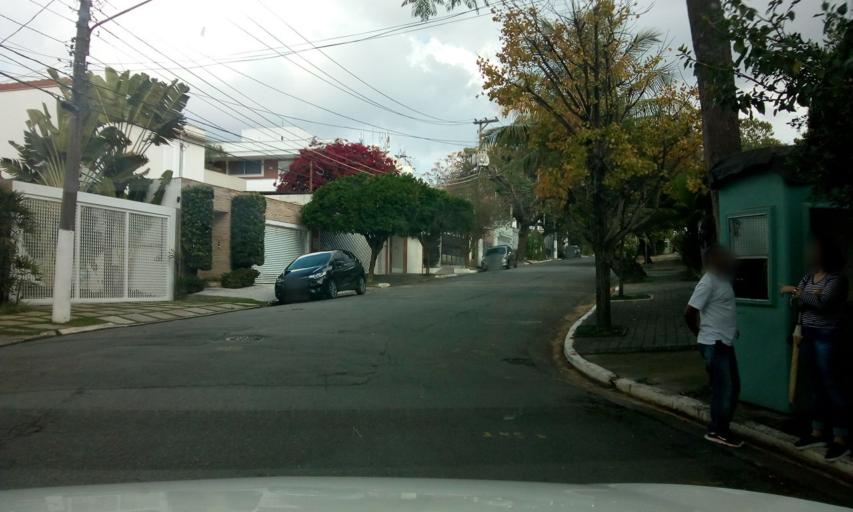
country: BR
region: Sao Paulo
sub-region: Sao Paulo
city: Sao Paulo
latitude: -23.6023
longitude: -46.6526
